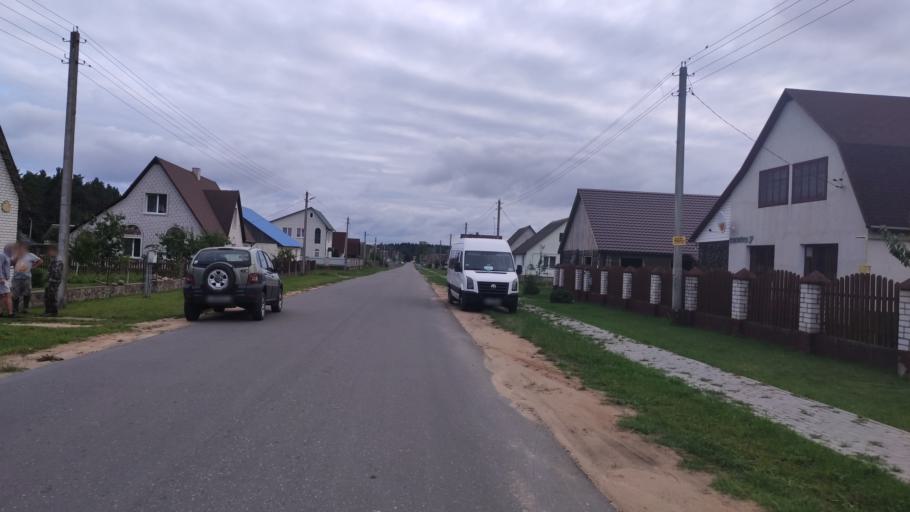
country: BY
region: Minsk
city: Narach
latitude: 54.9306
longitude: 26.6983
